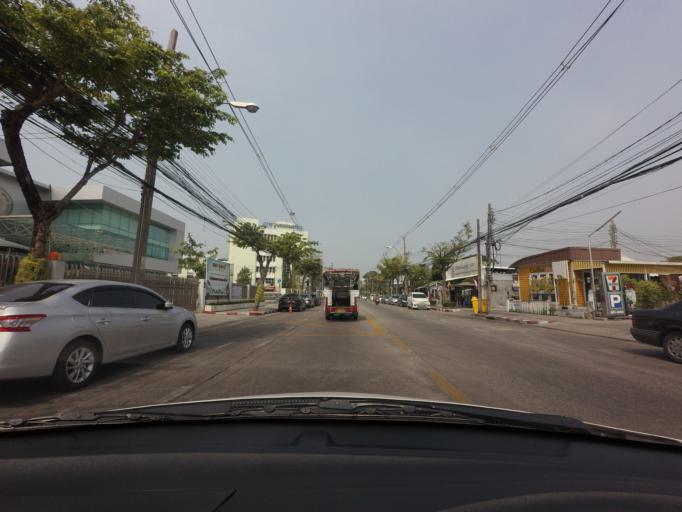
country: TH
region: Bangkok
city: Bangkok Noi
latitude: 13.7708
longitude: 100.4685
